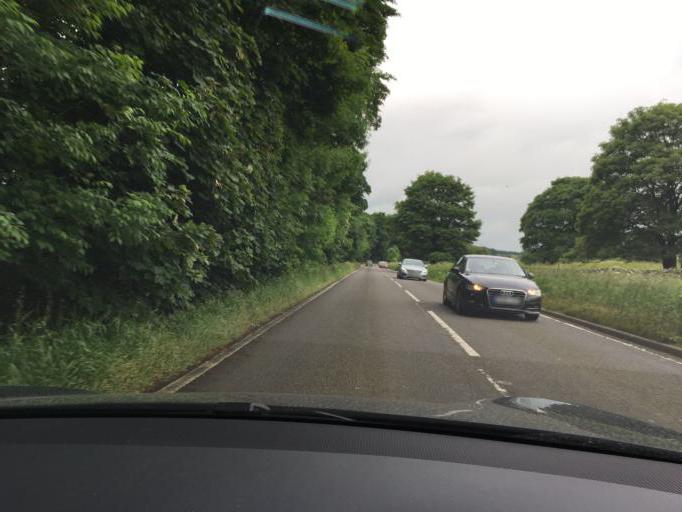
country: GB
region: England
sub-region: Derbyshire
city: High Peak
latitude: 53.3145
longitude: -1.8427
